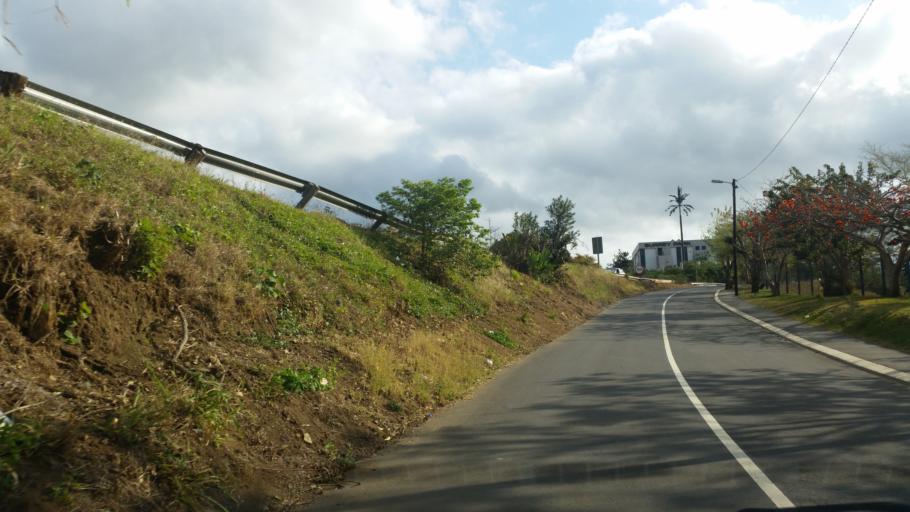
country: ZA
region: KwaZulu-Natal
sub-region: eThekwini Metropolitan Municipality
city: Berea
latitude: -29.8304
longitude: 30.9549
